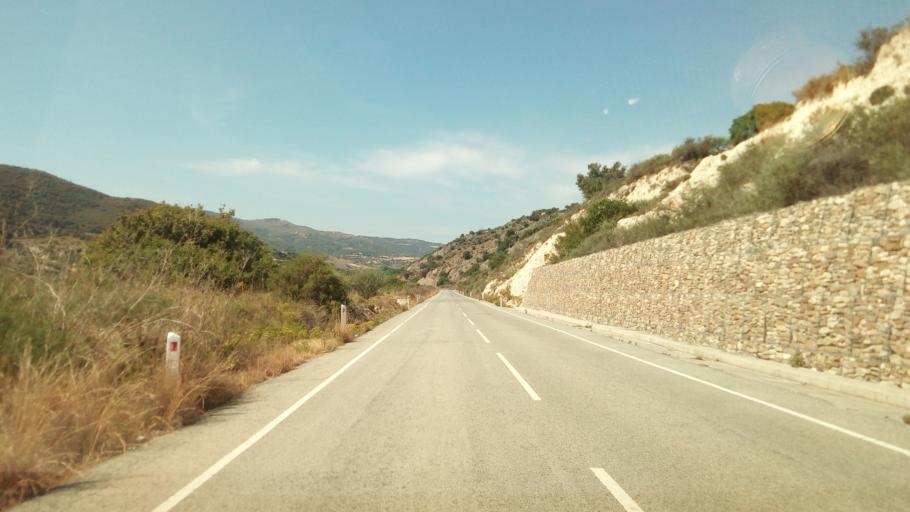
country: CY
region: Limassol
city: Pachna
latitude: 34.8054
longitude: 32.7111
